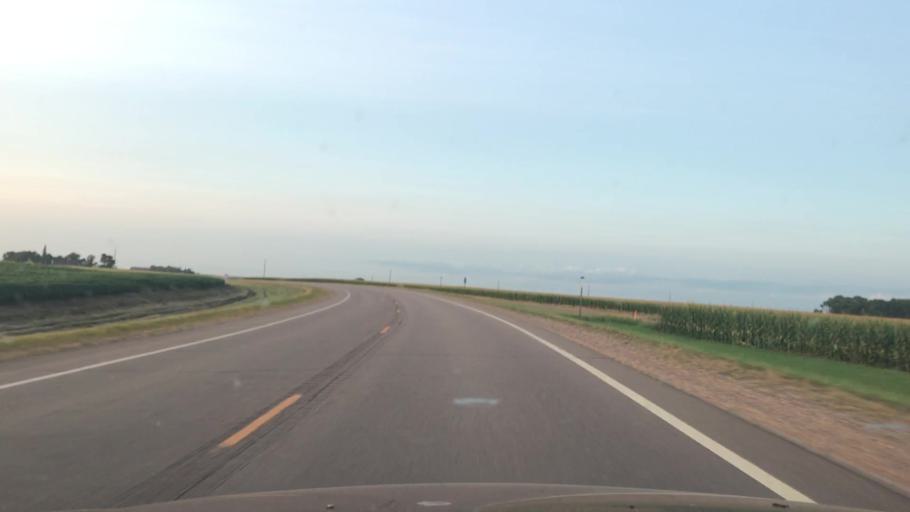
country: US
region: Minnesota
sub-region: Redwood County
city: Redwood Falls
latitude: 44.4195
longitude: -95.1187
